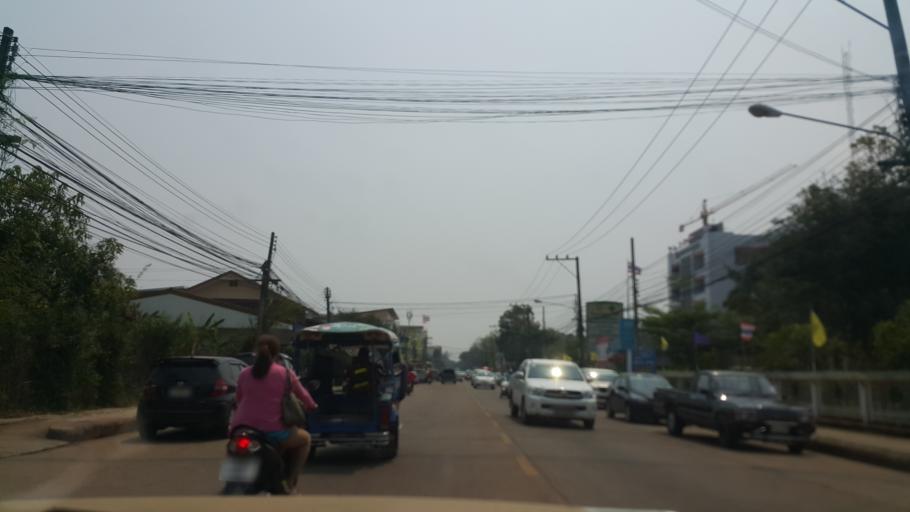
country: TH
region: Nakhon Phanom
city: Nakhon Phanom
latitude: 17.4149
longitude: 104.7777
